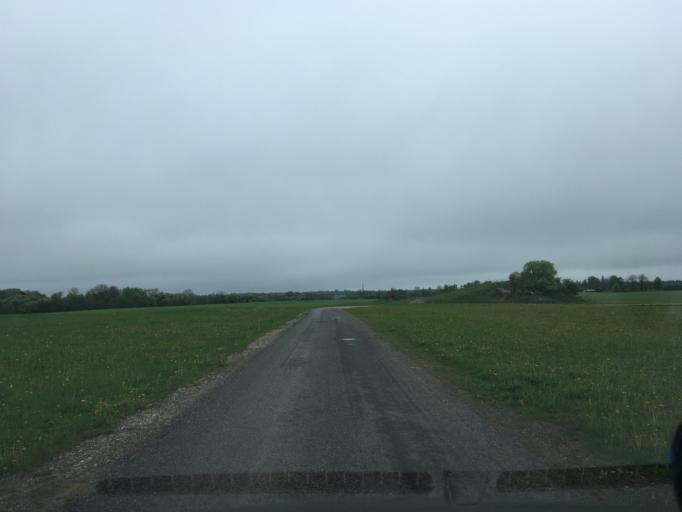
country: EE
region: Harju
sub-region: Rae vald
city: Vaida
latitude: 59.1851
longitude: 25.1066
